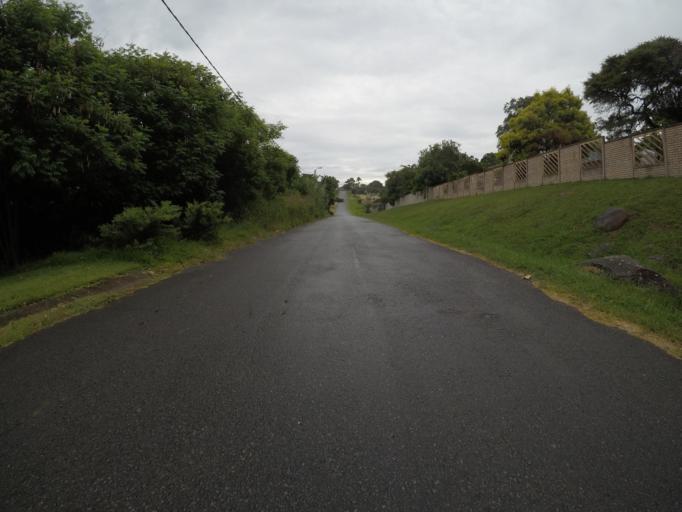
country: ZA
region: Eastern Cape
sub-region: Buffalo City Metropolitan Municipality
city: East London
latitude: -32.9637
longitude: 27.8467
